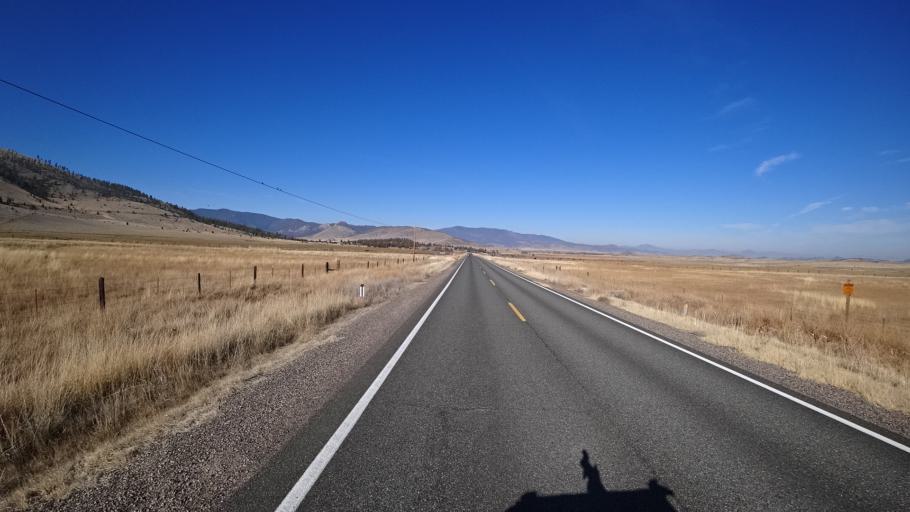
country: US
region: California
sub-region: Siskiyou County
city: Weed
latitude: 41.4848
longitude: -122.4995
